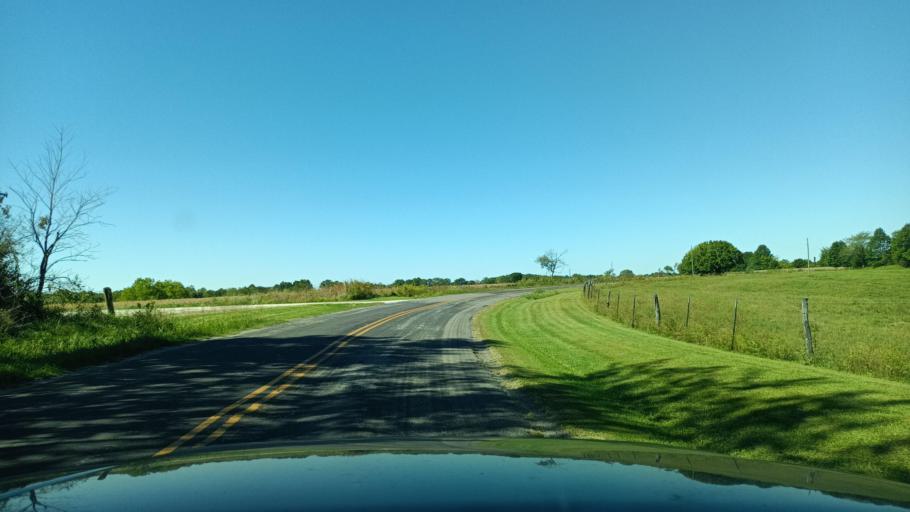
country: US
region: Missouri
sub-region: Scotland County
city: Memphis
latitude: 40.3534
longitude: -92.2673
